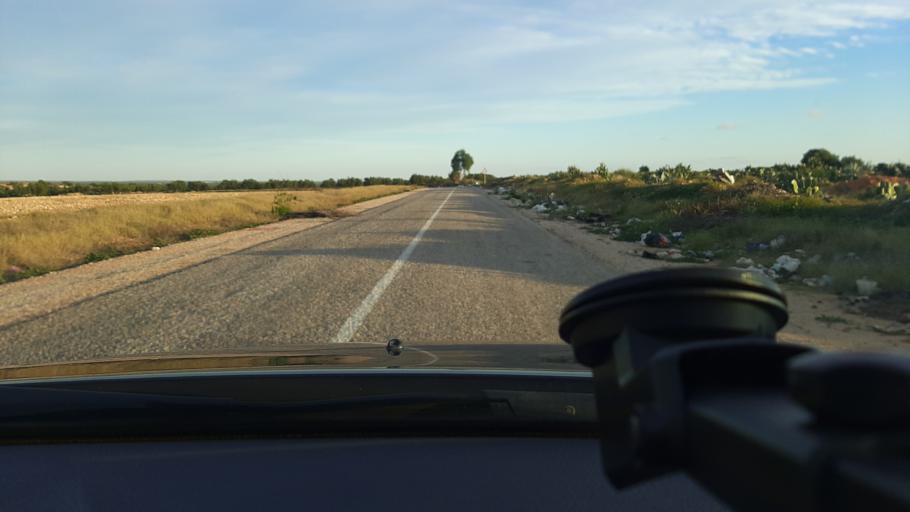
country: TN
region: Safaqis
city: Sfax
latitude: 34.9542
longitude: 10.5491
